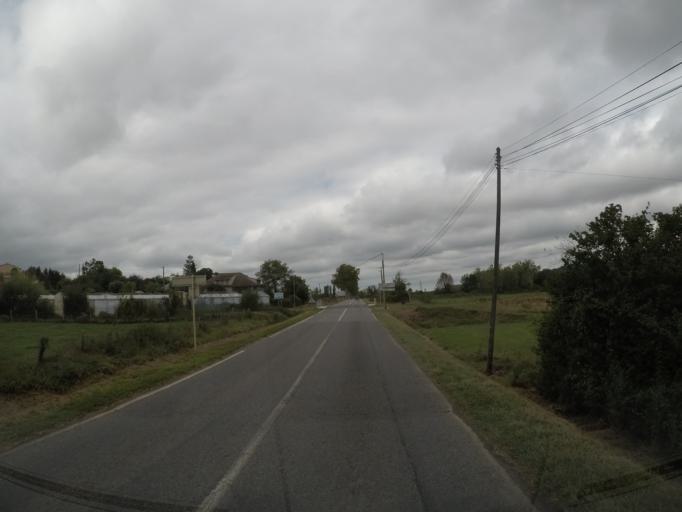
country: FR
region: Midi-Pyrenees
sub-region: Departement de l'Ariege
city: Lezat-sur-Leze
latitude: 43.2320
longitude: 1.3752
